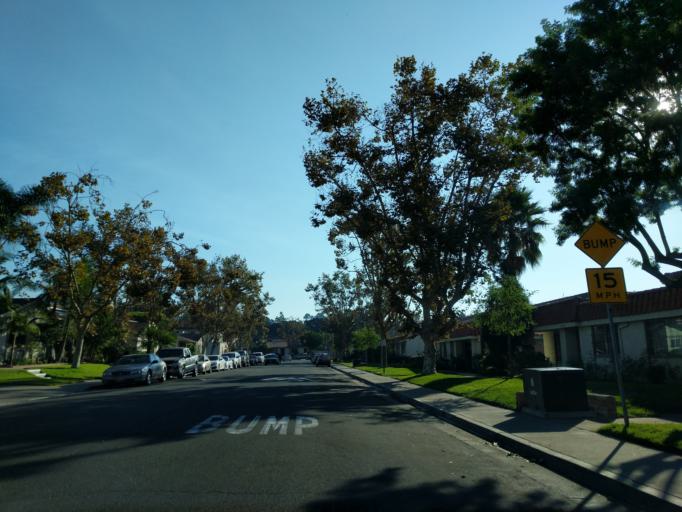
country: US
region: California
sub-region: Orange County
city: San Juan Capistrano
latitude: 33.5081
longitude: -117.6685
